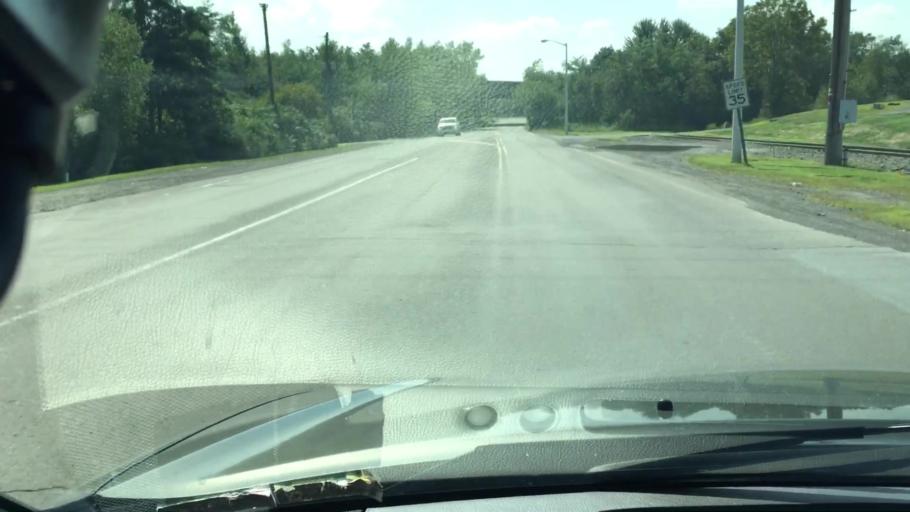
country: US
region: Pennsylvania
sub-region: Luzerne County
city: Ashley
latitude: 41.2013
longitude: -75.9227
